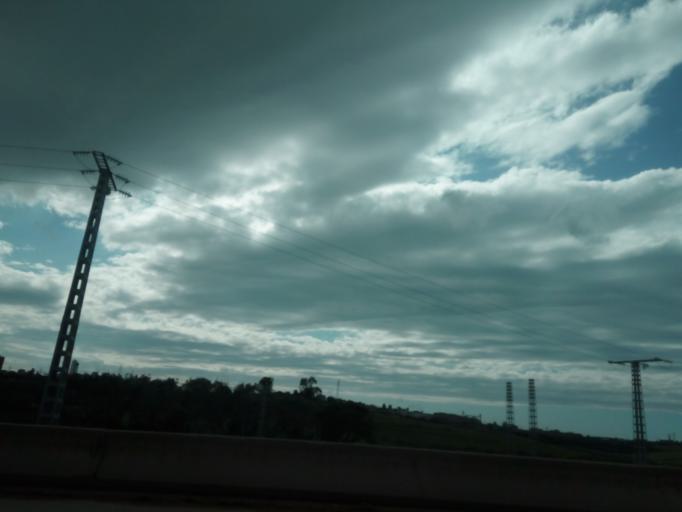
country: DZ
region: Tipaza
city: Douera
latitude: 36.6888
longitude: 2.9563
